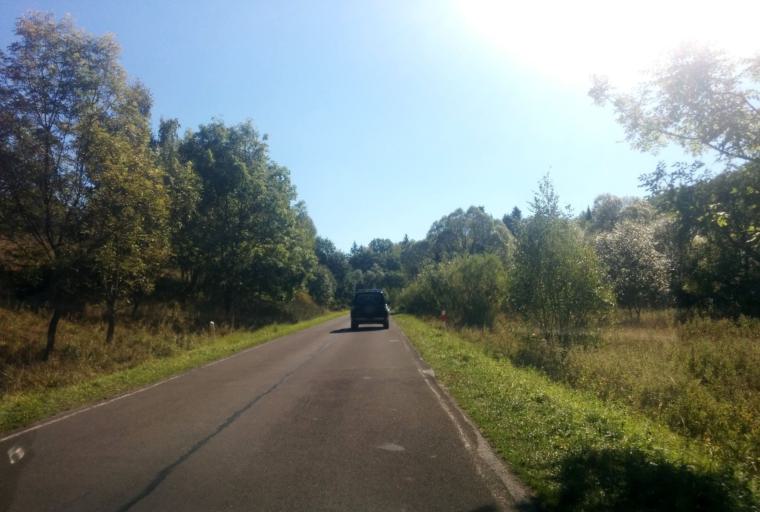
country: PL
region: Subcarpathian Voivodeship
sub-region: Powiat bieszczadzki
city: Lutowiska
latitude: 49.1453
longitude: 22.5267
